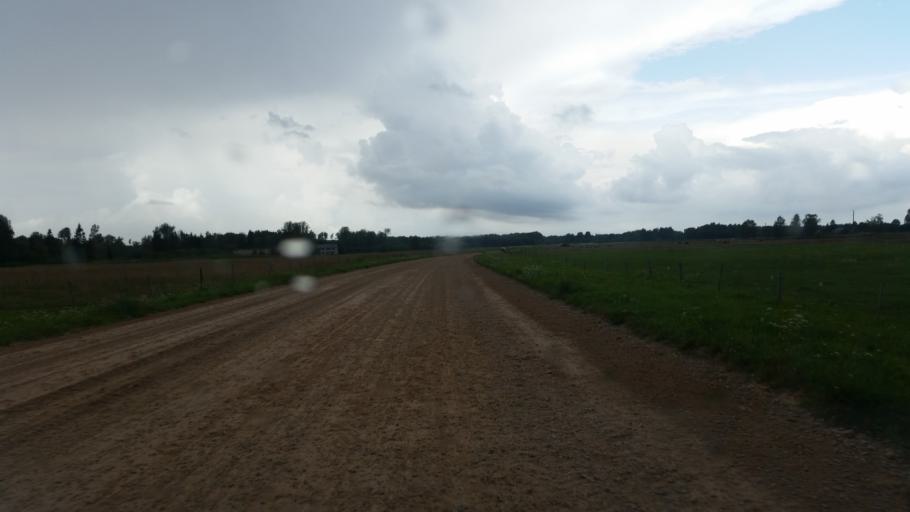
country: LV
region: Vecumnieki
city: Vecumnieki
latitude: 56.4263
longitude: 24.4716
